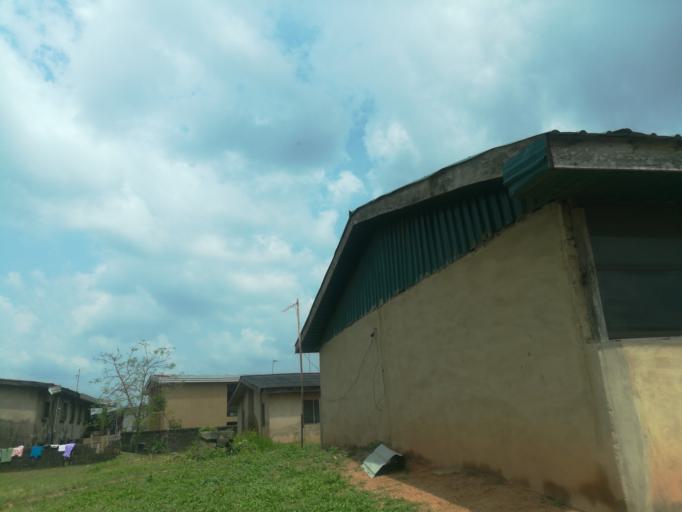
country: NG
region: Oyo
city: Ibadan
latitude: 7.4375
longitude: 3.9389
